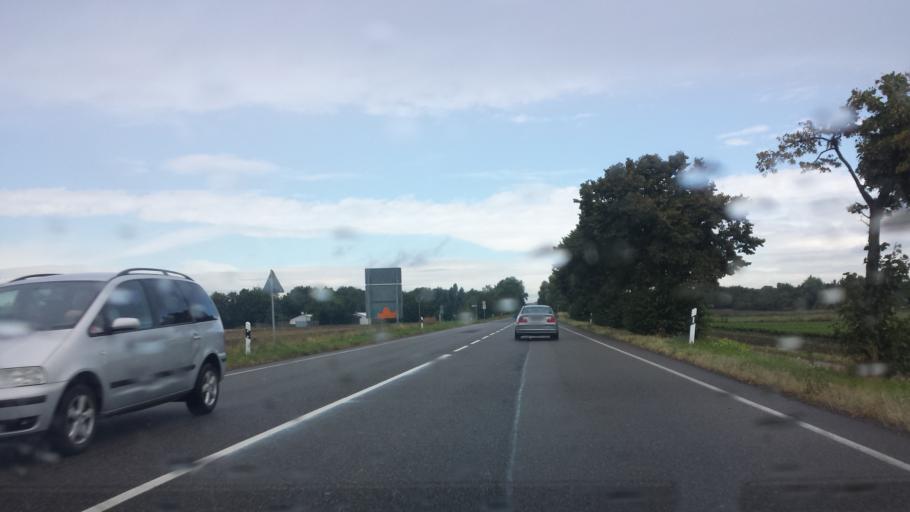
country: DE
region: Rheinland-Pfalz
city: Bobenheim-Roxheim
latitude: 49.6053
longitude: 8.3583
